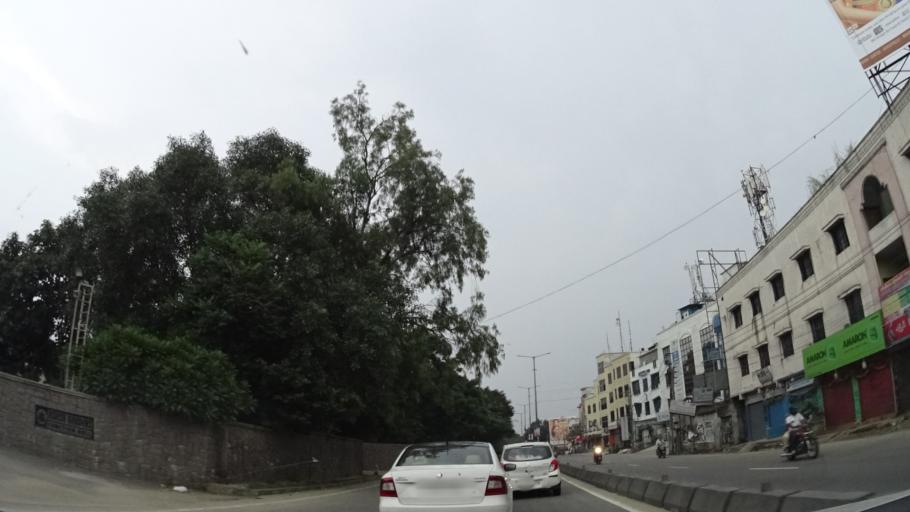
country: IN
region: Telangana
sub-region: Rangareddi
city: Quthbullapur
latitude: 17.4573
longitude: 78.4784
